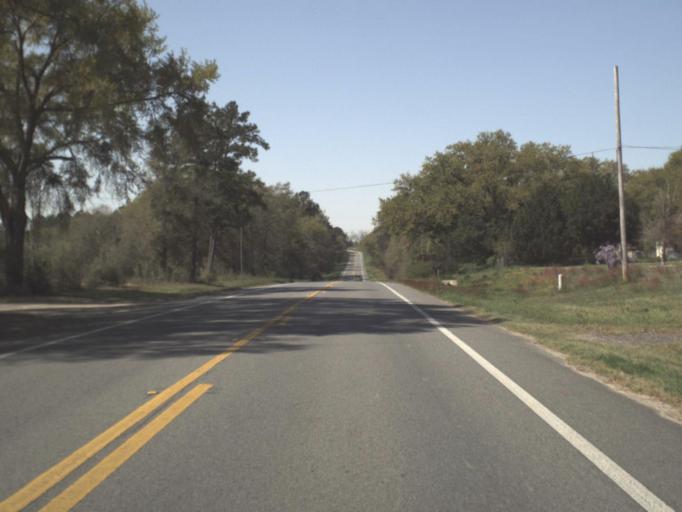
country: US
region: Florida
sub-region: Jackson County
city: Graceville
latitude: 30.9024
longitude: -85.4478
